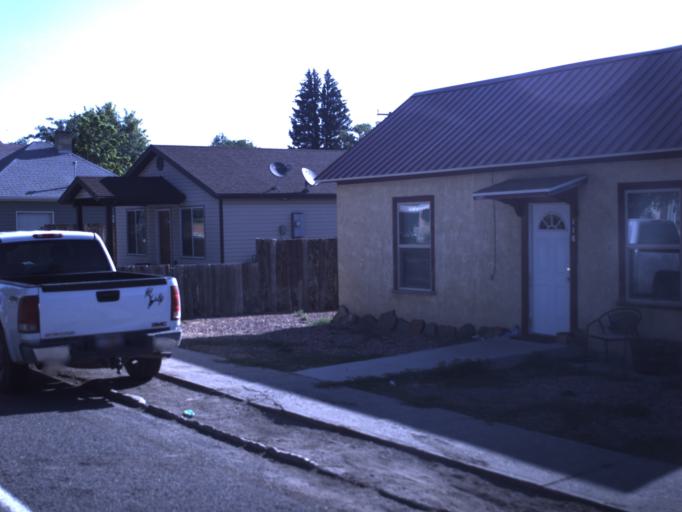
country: US
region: Utah
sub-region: Beaver County
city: Milford
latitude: 38.3983
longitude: -113.0105
